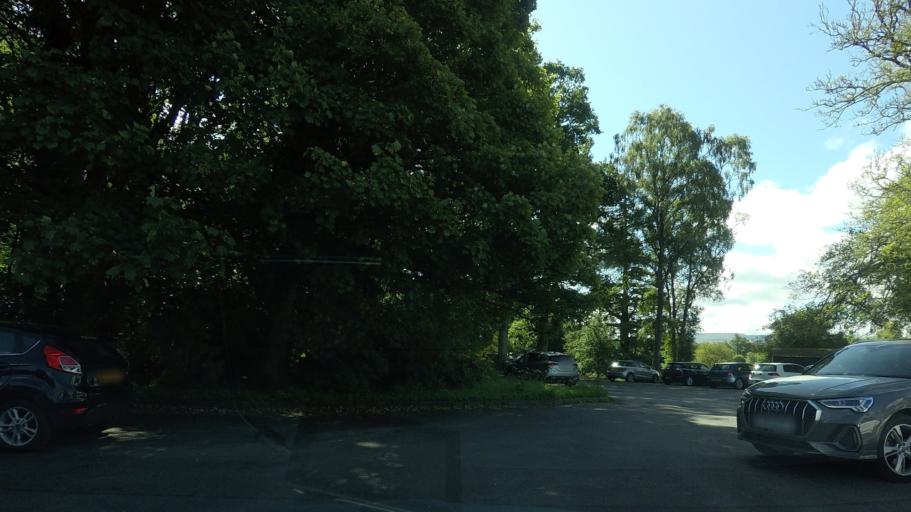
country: GB
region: Scotland
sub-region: Stirling
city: Killearn
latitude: 56.0675
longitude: -4.4794
